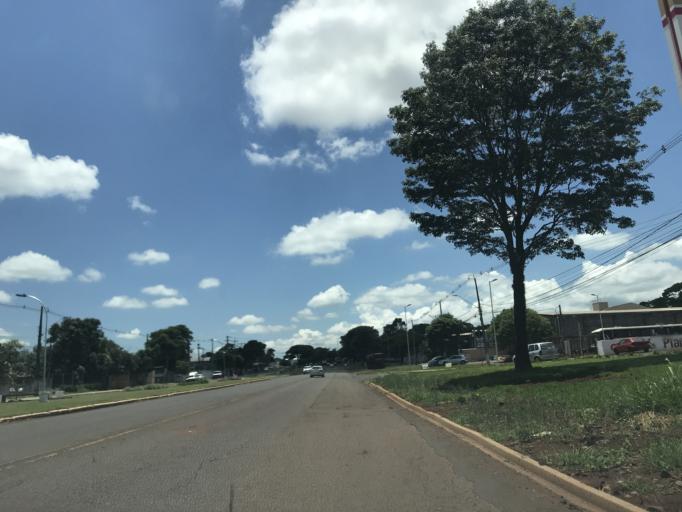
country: BR
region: Parana
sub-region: Marialva
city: Marialva
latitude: -23.4766
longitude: -51.8107
